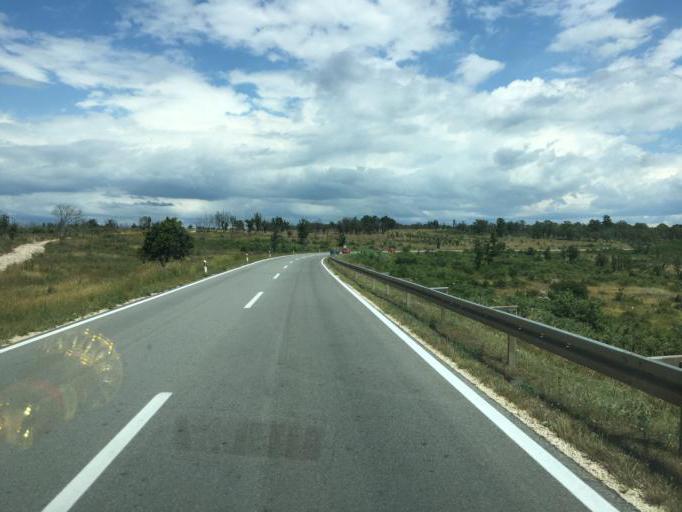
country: HR
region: Istarska
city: Karojba
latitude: 45.2135
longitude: 13.7750
